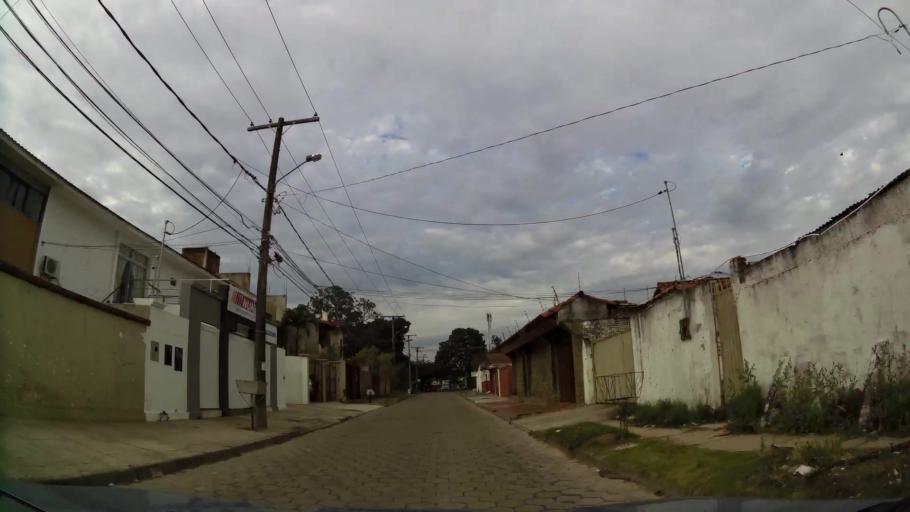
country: BO
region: Santa Cruz
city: Santa Cruz de la Sierra
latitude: -17.7570
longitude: -63.1714
